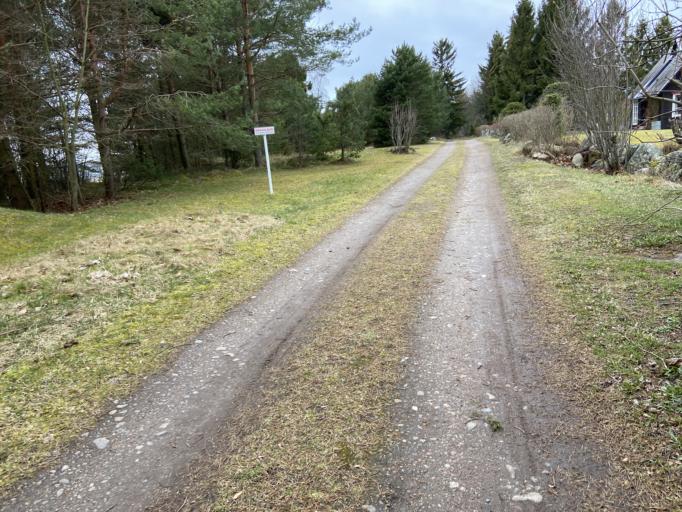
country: EE
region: Harju
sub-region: Loksa linn
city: Loksa
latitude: 59.6529
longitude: 25.6761
